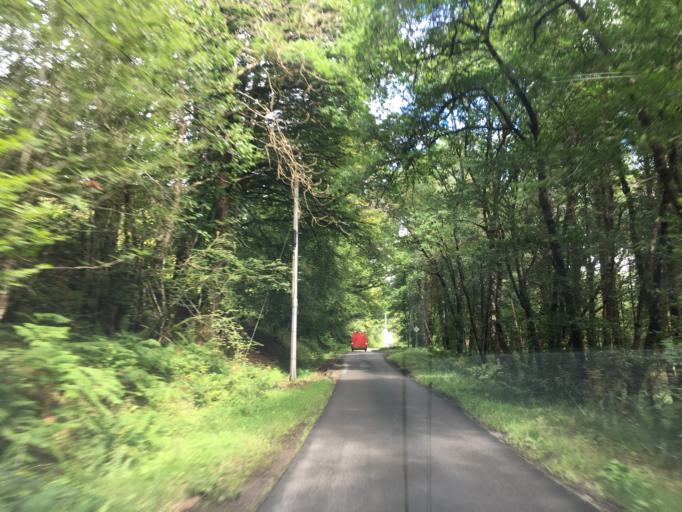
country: GB
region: Scotland
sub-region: Argyll and Bute
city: Oban
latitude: 56.2994
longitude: -5.2481
